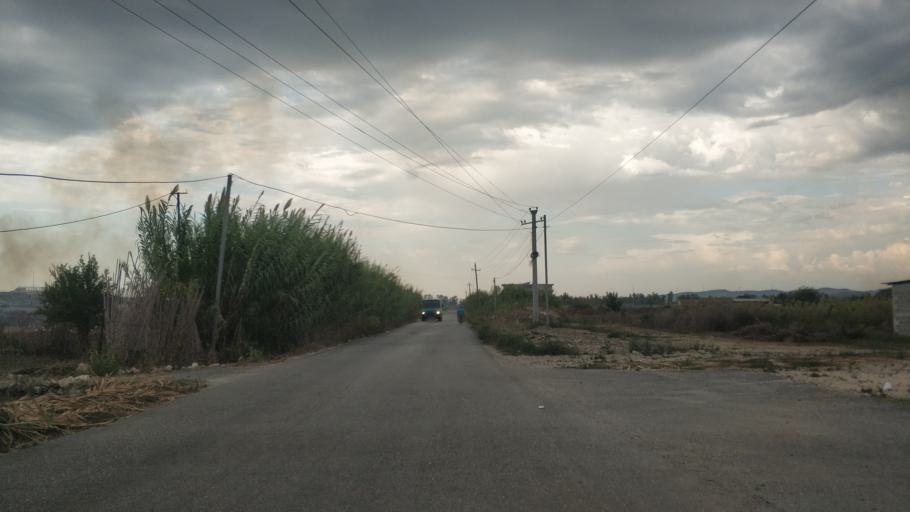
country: AL
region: Fier
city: Fier
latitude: 40.7452
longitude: 19.5595
